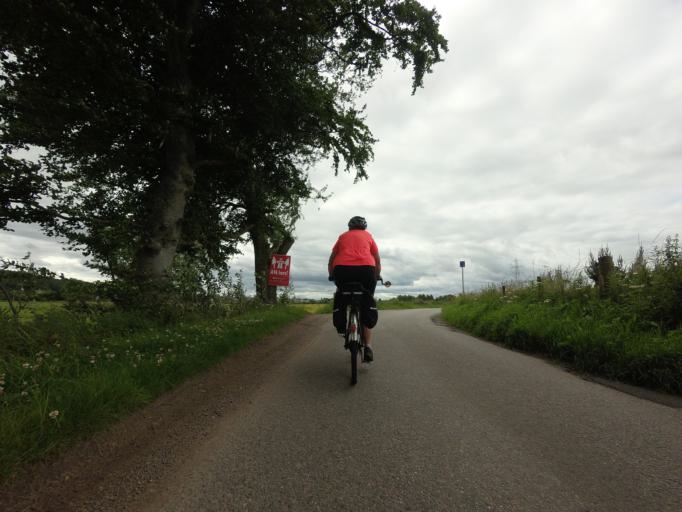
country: GB
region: Scotland
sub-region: Moray
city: Forres
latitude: 57.6200
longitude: -3.6140
